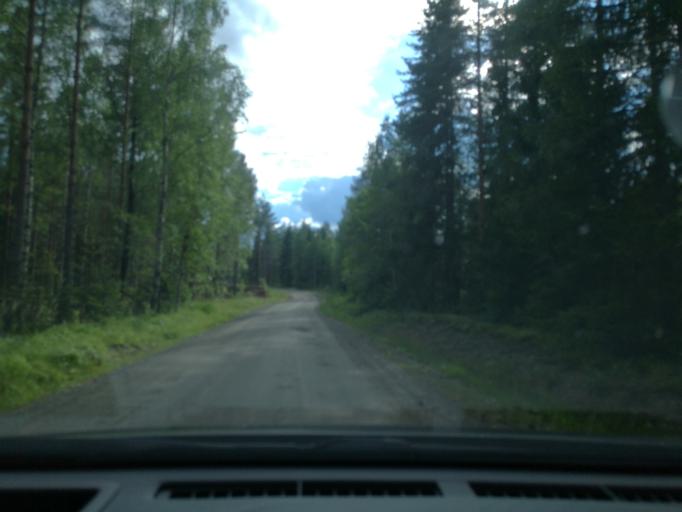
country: SE
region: Vaestmanland
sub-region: Surahammars Kommun
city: Ramnas
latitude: 59.8174
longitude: 16.2469
